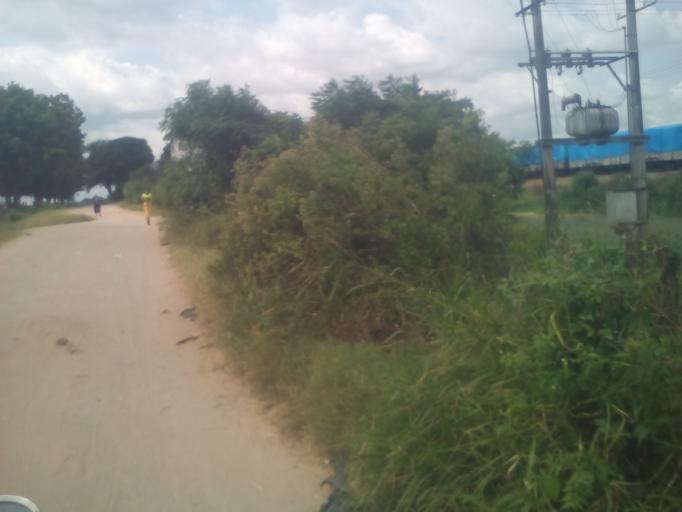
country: TZ
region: Dar es Salaam
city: Dar es Salaam
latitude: -6.8670
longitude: 39.2349
